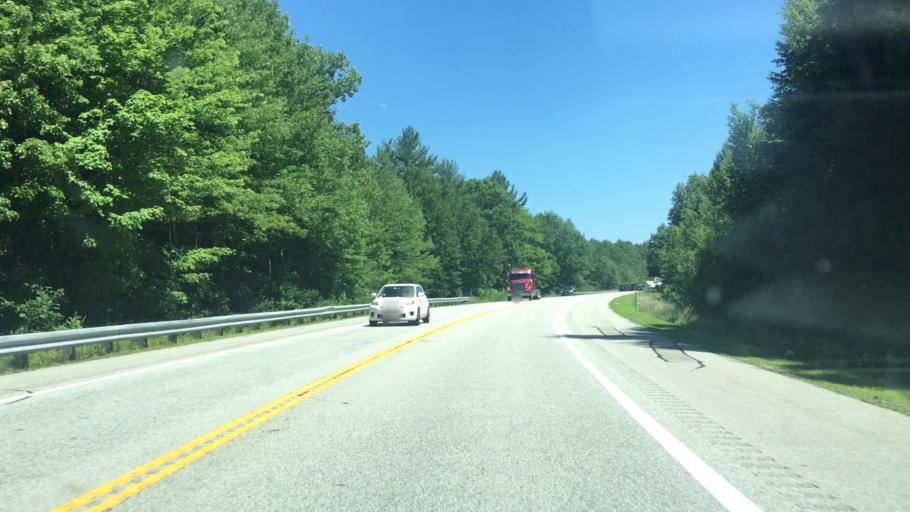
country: US
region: New Hampshire
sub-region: Merrimack County
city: Contoocook
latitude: 43.1802
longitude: -71.7339
